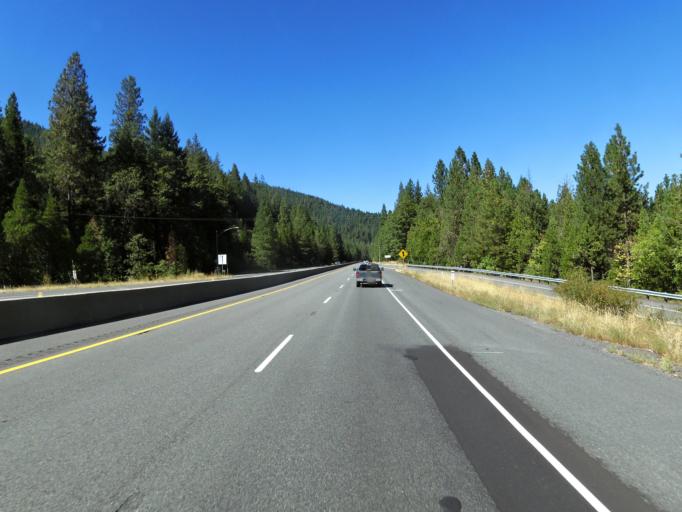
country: US
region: California
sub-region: Siskiyou County
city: Dunsmuir
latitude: 41.1634
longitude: -122.2975
